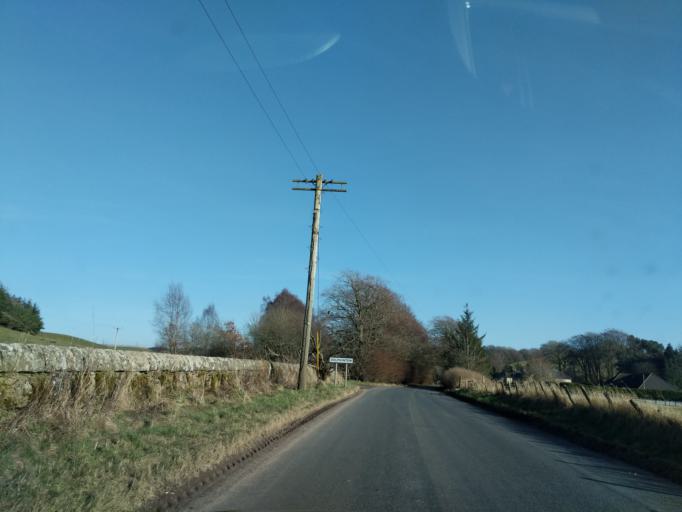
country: GB
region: Scotland
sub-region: The Scottish Borders
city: West Linton
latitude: 55.7175
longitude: -3.4219
